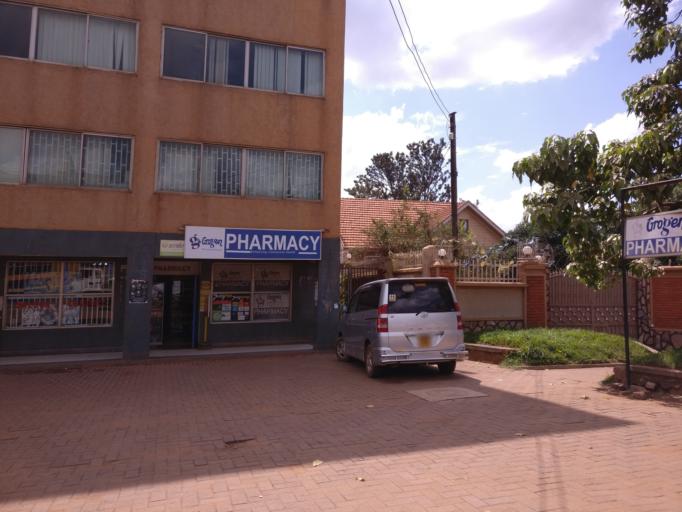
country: UG
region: Central Region
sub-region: Kampala District
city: Kampala
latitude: 0.3059
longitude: 32.5623
